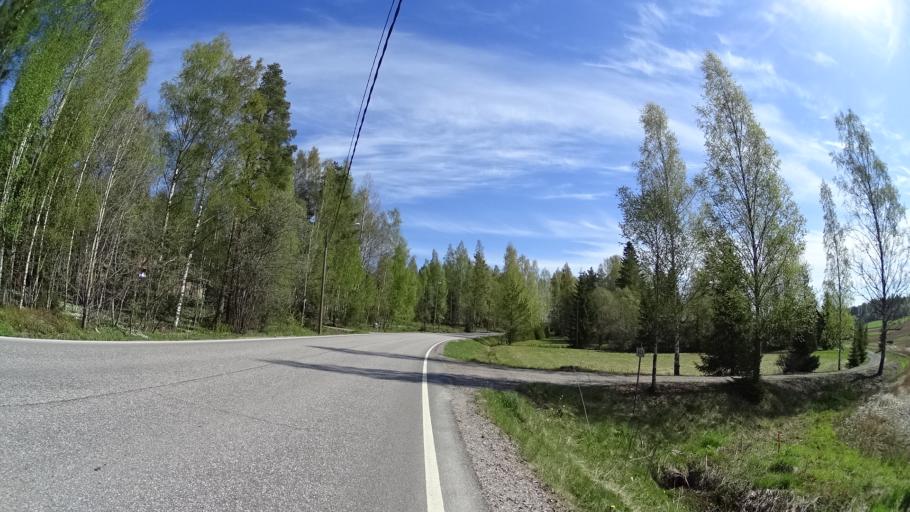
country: FI
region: Uusimaa
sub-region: Helsinki
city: Nurmijaervi
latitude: 60.3961
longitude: 24.8239
